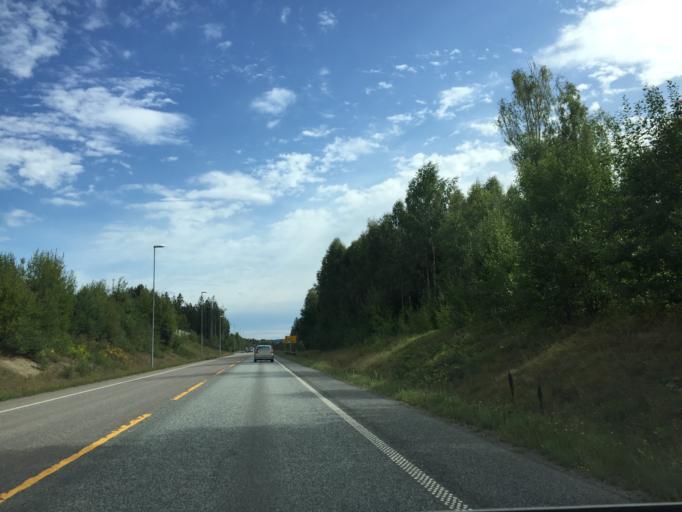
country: NO
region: Akershus
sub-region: Ski
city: Ski
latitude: 59.7103
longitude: 10.8191
